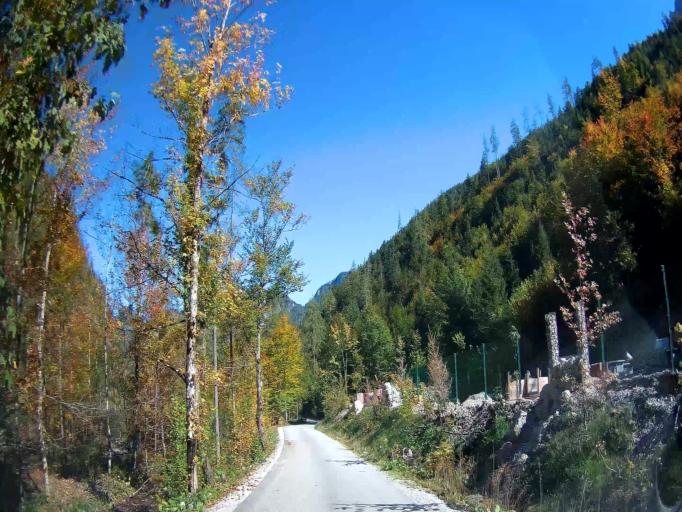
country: AT
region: Salzburg
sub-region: Politischer Bezirk Zell am See
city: Sankt Martin bei Lofer
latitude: 47.5237
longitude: 12.7110
